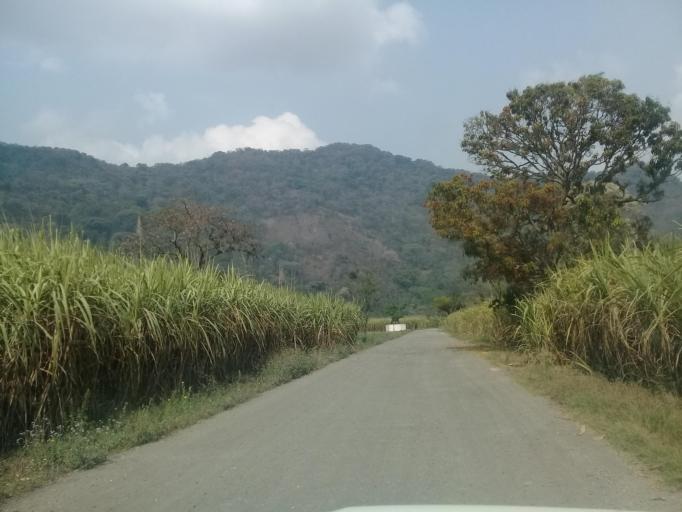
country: MX
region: Veracruz
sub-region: Ixtaczoquitlan
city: Capoluca
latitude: 18.8117
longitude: -96.9902
